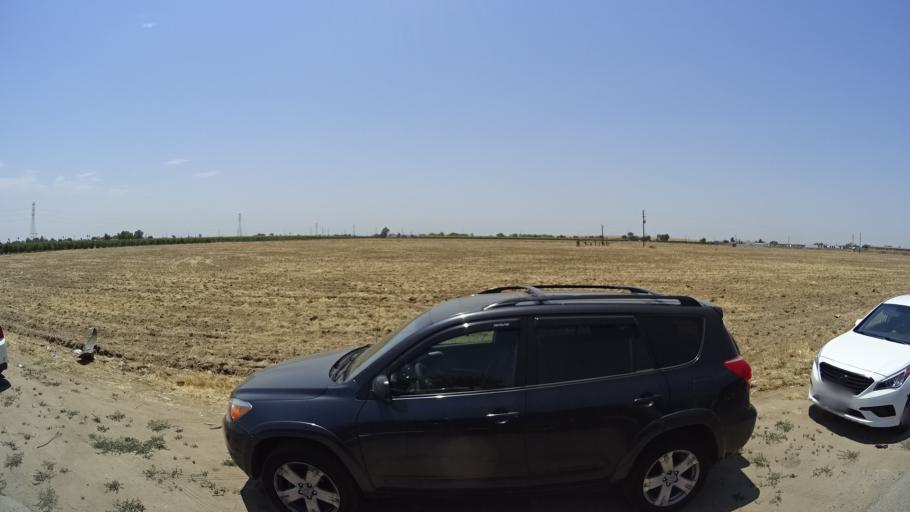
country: US
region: California
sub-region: Fresno County
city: West Park
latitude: 36.7139
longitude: -119.8238
